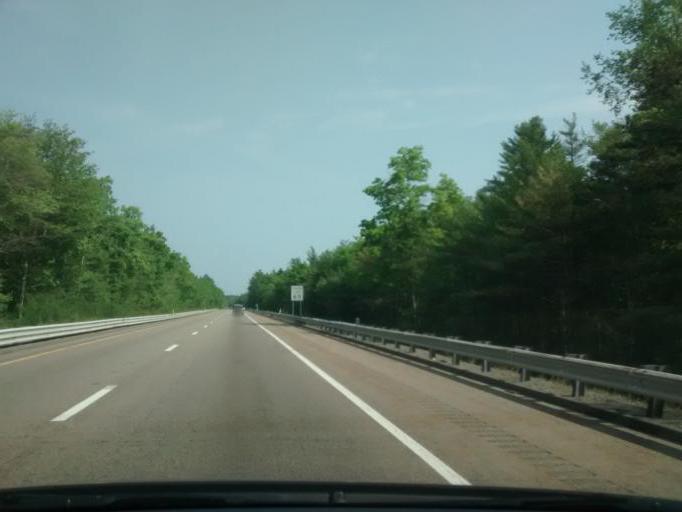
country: US
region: Massachusetts
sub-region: Plymouth County
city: West Wareham
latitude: 41.8223
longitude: -70.8059
